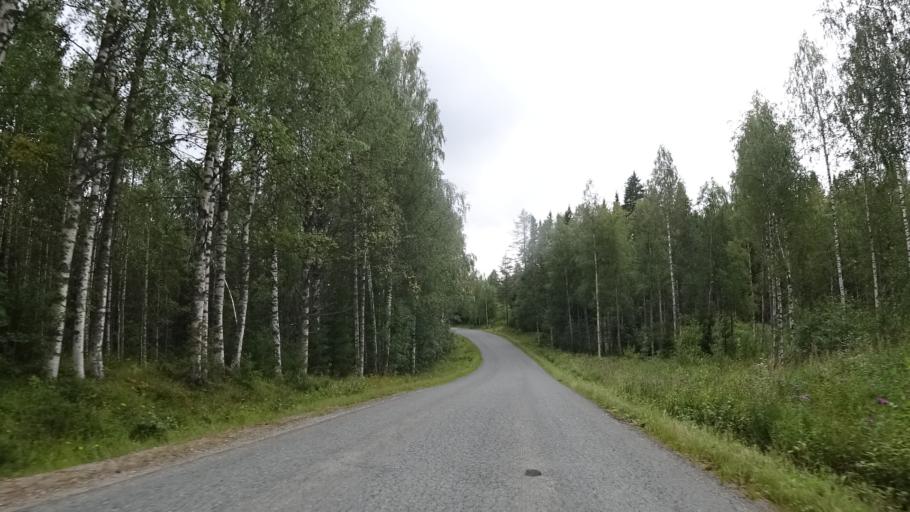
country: FI
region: North Karelia
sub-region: Joensuu
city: Ilomantsi
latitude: 62.9510
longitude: 31.2956
